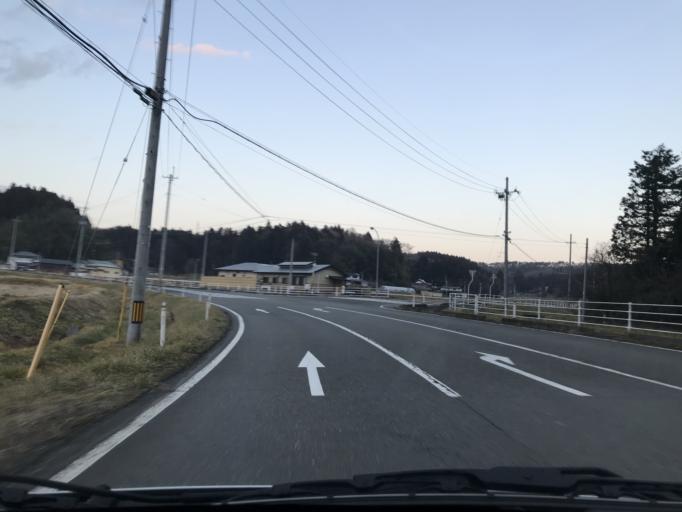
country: JP
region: Iwate
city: Ichinoseki
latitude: 38.8071
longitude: 141.1180
